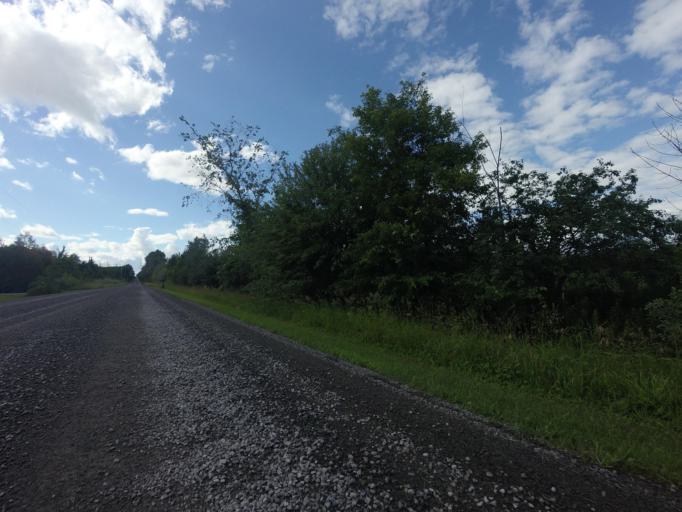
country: CA
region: Ontario
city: Arnprior
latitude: 45.3331
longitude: -76.1843
